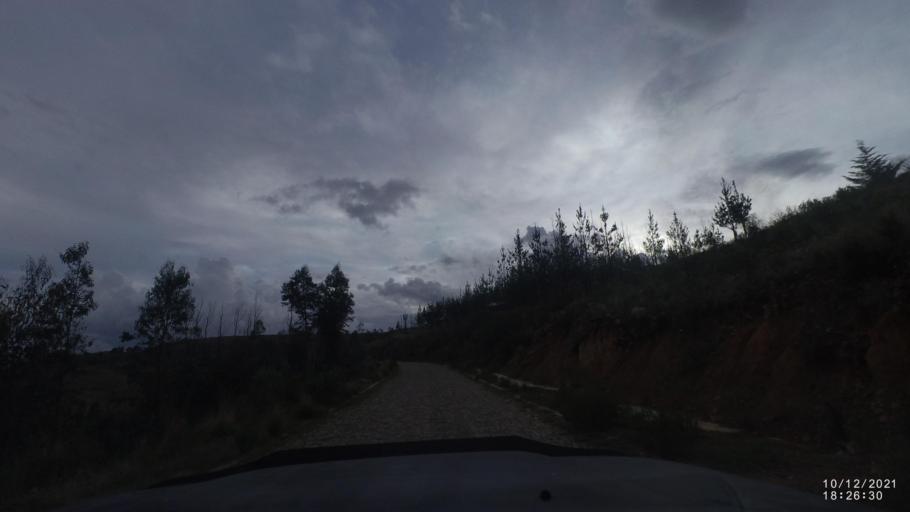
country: BO
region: Cochabamba
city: Tarata
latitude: -17.7971
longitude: -65.9734
